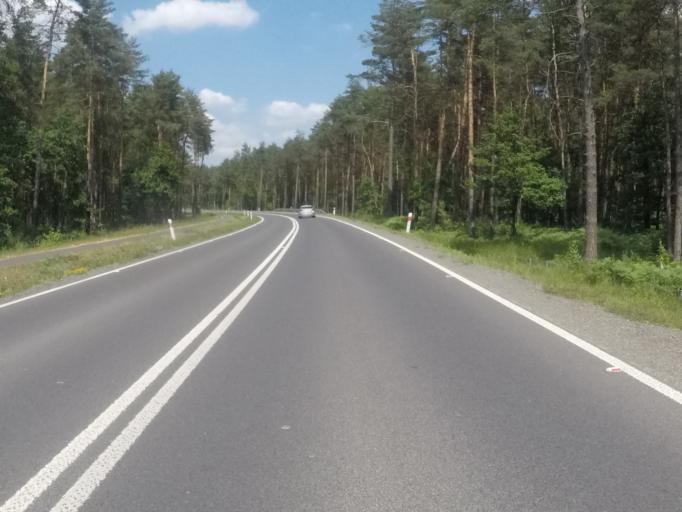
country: PL
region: Lesser Poland Voivodeship
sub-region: Powiat chrzanowski
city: Chrzanow
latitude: 50.1337
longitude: 19.3728
